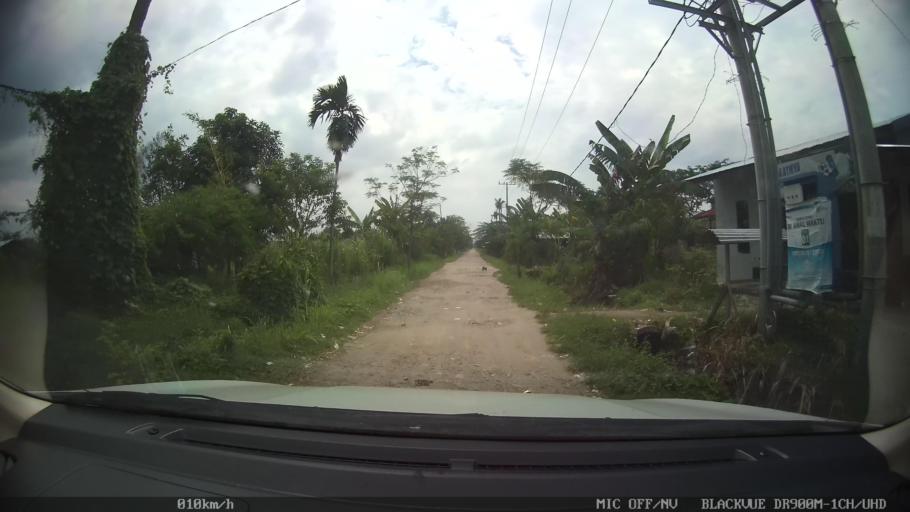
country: ID
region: North Sumatra
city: Sunggal
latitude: 3.6238
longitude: 98.6022
